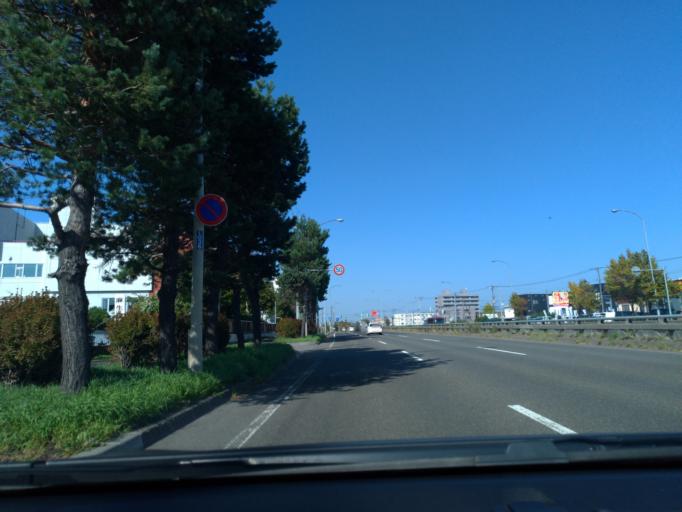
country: JP
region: Hokkaido
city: Sapporo
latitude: 43.1133
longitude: 141.3435
